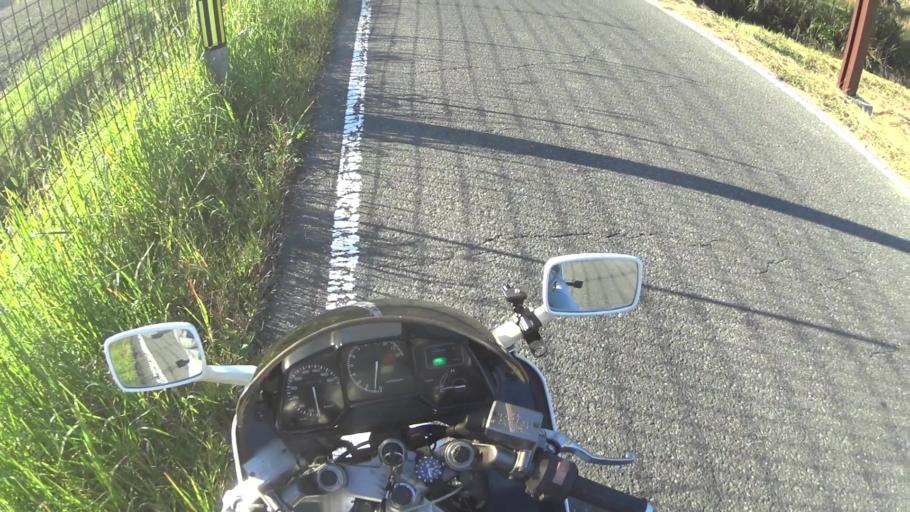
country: JP
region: Hyogo
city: Toyooka
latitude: 35.6095
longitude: 134.8876
